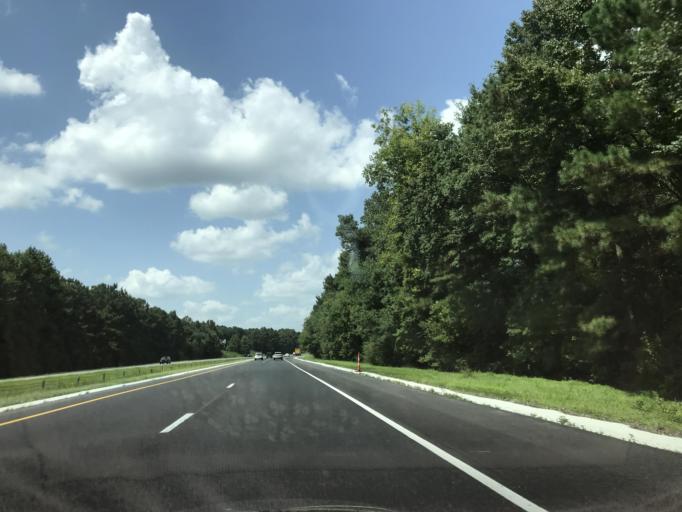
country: US
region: North Carolina
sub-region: Duplin County
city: Warsaw
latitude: 34.9556
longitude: -78.0974
